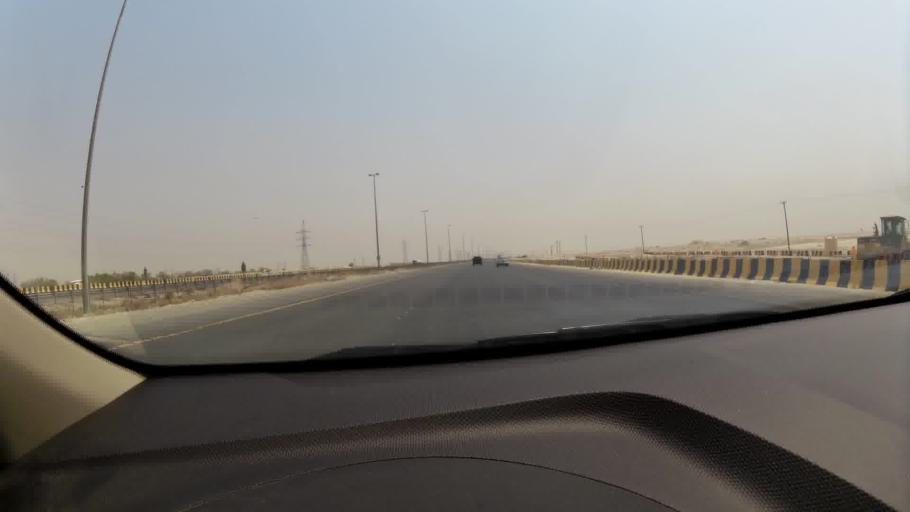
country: KW
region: Al Asimah
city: Ar Rabiyah
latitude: 29.2272
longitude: 47.8848
